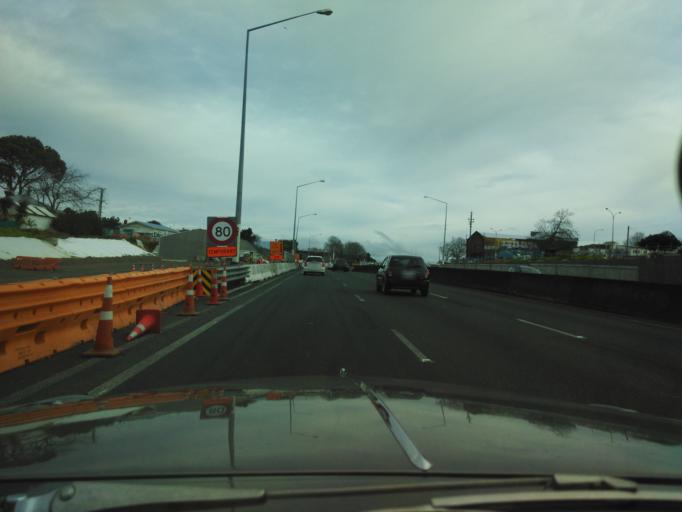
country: NZ
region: Auckland
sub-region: Auckland
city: Rosebank
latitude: -36.8709
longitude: 174.7134
